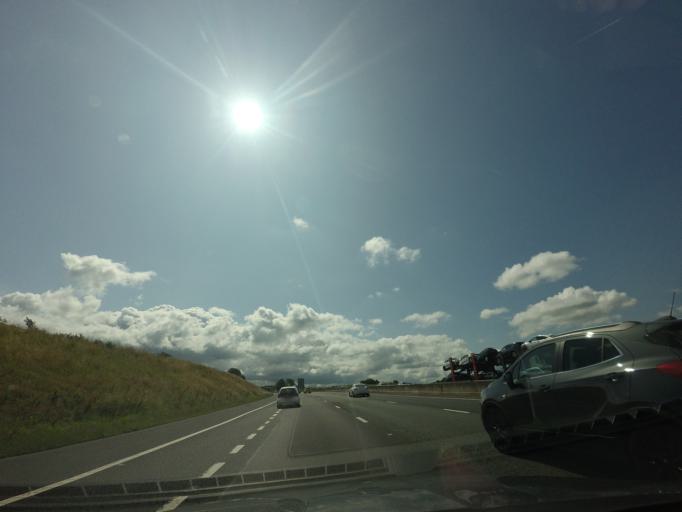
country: GB
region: England
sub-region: Lancashire
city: Bolton le Sands
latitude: 54.0622
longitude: -2.7713
